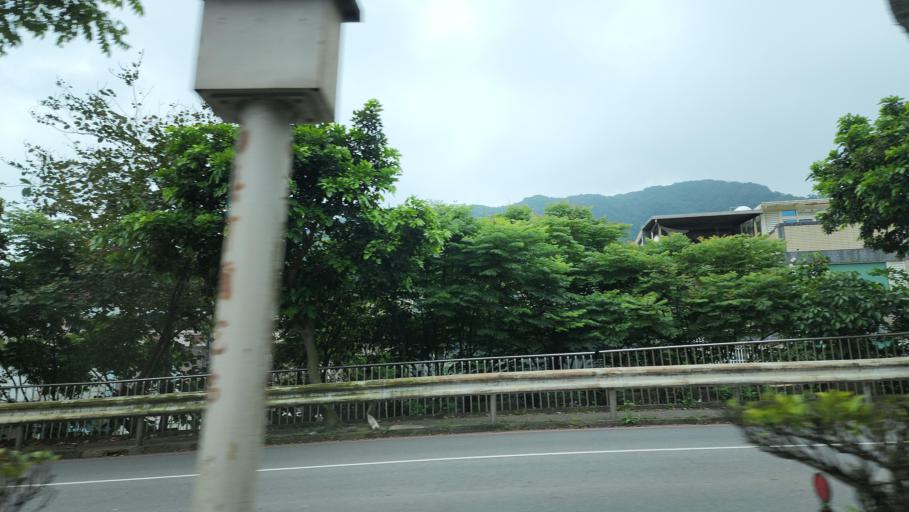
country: TW
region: Taiwan
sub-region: Keelung
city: Keelung
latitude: 25.1576
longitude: 121.6946
